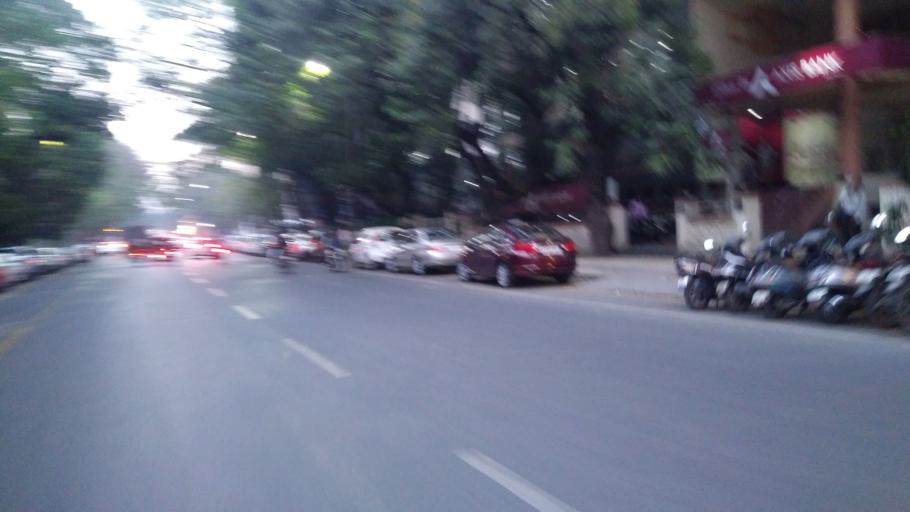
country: IN
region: Maharashtra
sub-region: Pune Division
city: Shivaji Nagar
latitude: 18.5230
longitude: 73.8410
